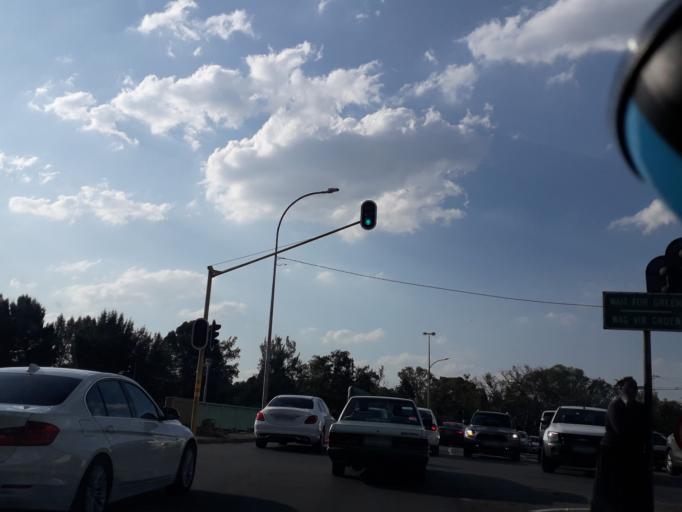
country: ZA
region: Gauteng
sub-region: City of Johannesburg Metropolitan Municipality
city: Johannesburg
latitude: -26.1396
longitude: 28.0674
